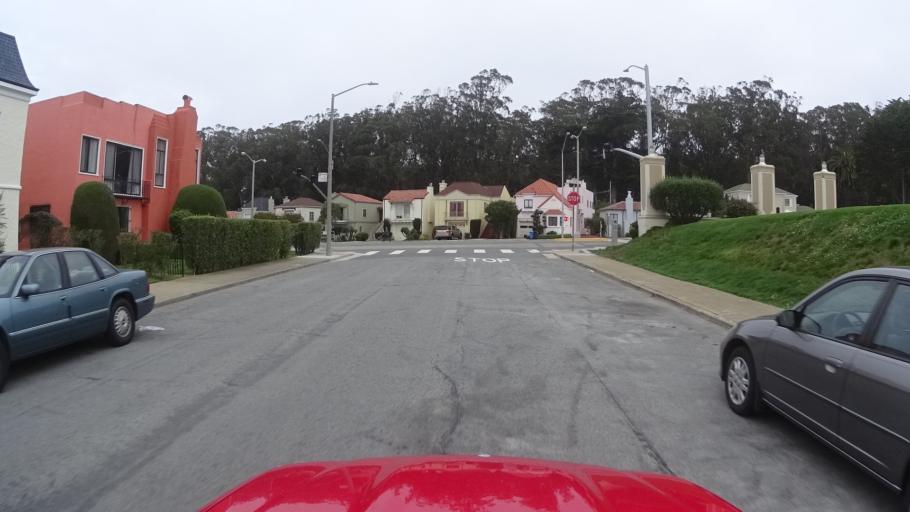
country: US
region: California
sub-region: San Mateo County
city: Daly City
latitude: 37.7341
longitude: -122.4794
